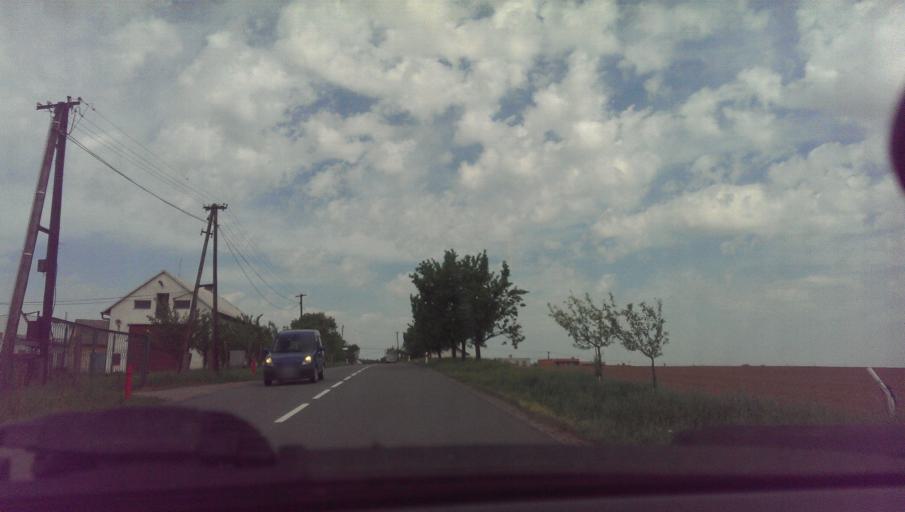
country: CZ
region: Zlin
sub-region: Okres Zlin
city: Otrokovice
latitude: 49.2496
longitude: 17.5434
